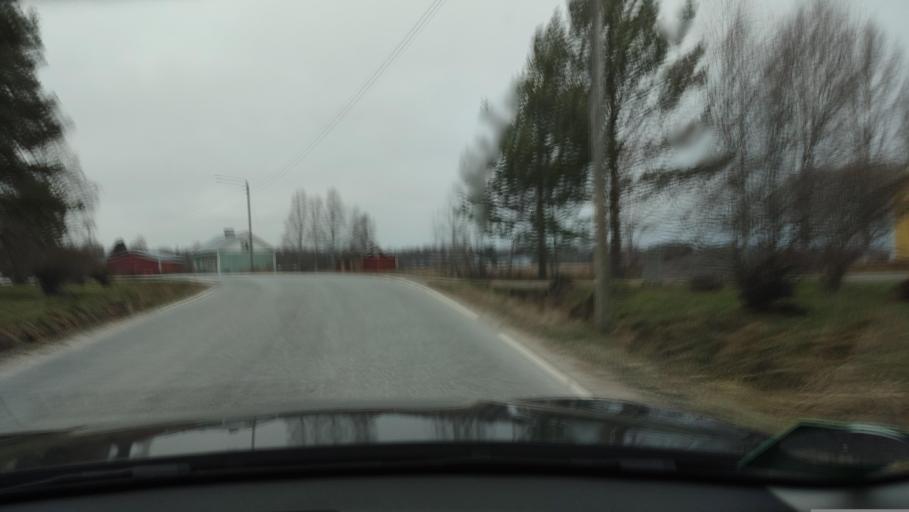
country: FI
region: Southern Ostrobothnia
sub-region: Suupohja
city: Karijoki
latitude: 62.2707
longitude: 21.7212
